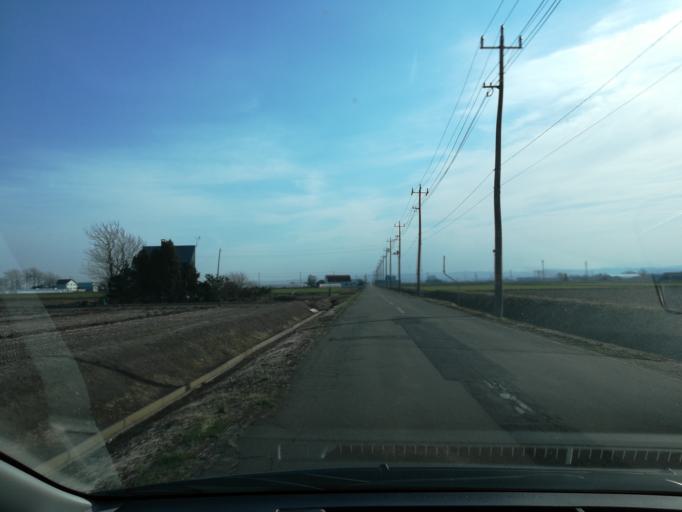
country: JP
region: Hokkaido
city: Ebetsu
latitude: 43.1579
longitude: 141.6431
